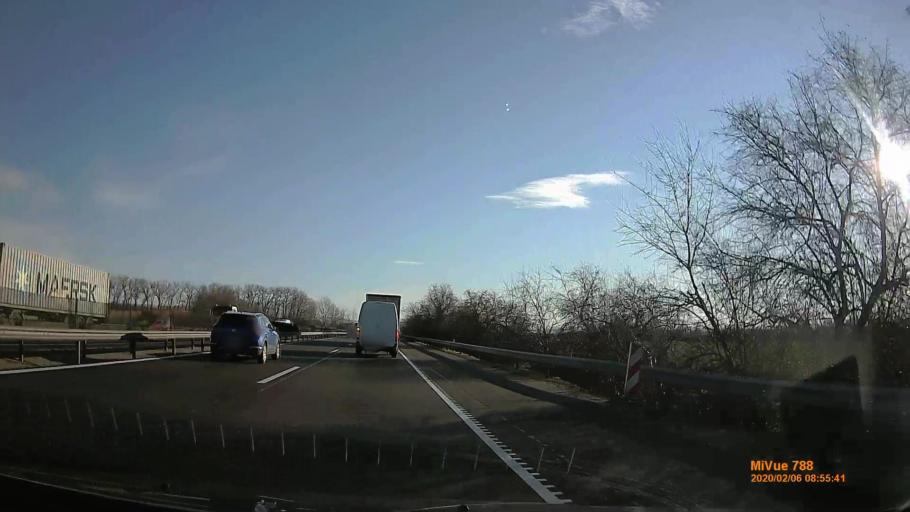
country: HU
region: Pest
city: Zsambek
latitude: 47.5100
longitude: 18.7171
